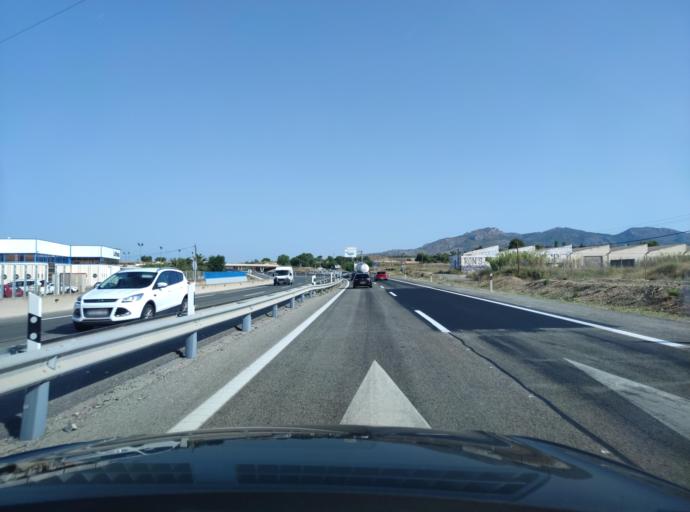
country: ES
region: Valencia
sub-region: Provincia de Alicante
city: Sax
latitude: 38.5454
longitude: -0.8134
